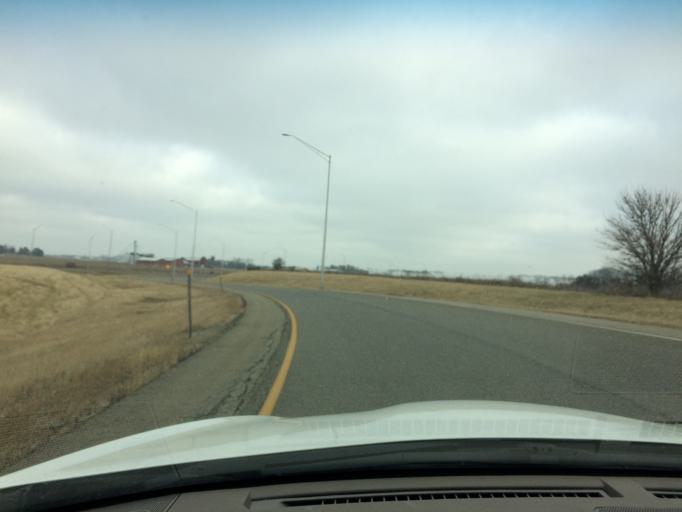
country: US
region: Illinois
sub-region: DeKalb County
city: Cortland
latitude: 41.8987
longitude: -88.7213
